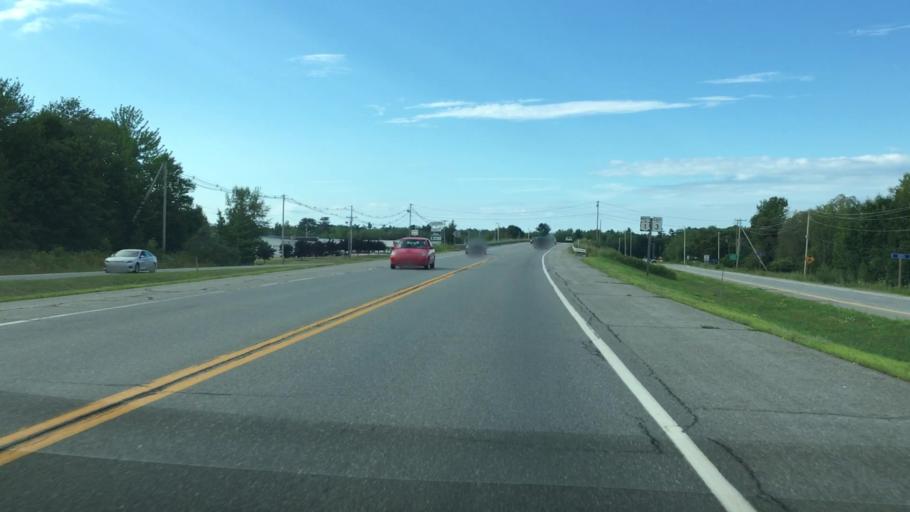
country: US
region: Maine
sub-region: Waldo County
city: Belfast
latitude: 44.4207
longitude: -69.0206
